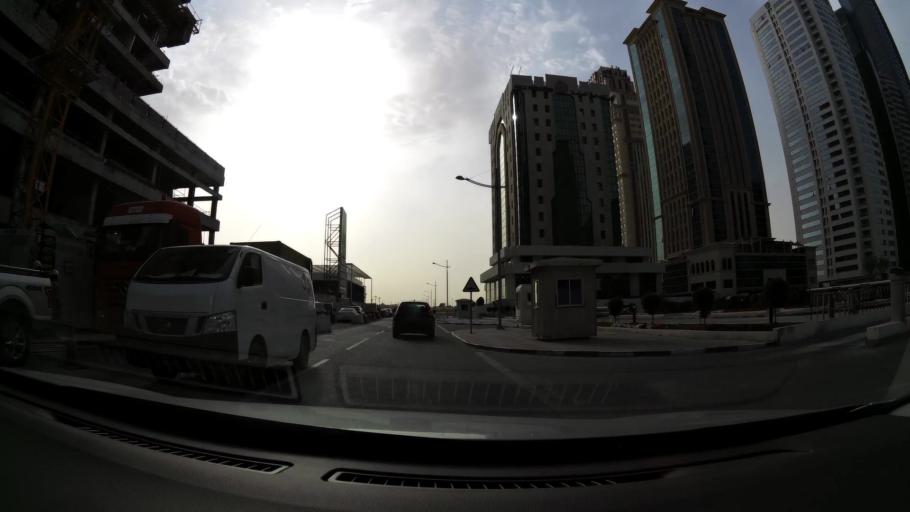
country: QA
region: Baladiyat ad Dawhah
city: Doha
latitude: 25.3239
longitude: 51.5255
